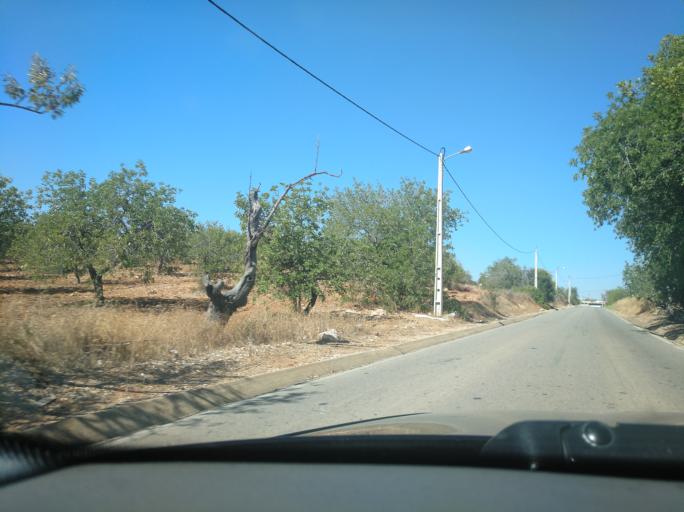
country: PT
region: Faro
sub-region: Faro
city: Faro
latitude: 37.0579
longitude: -7.9000
